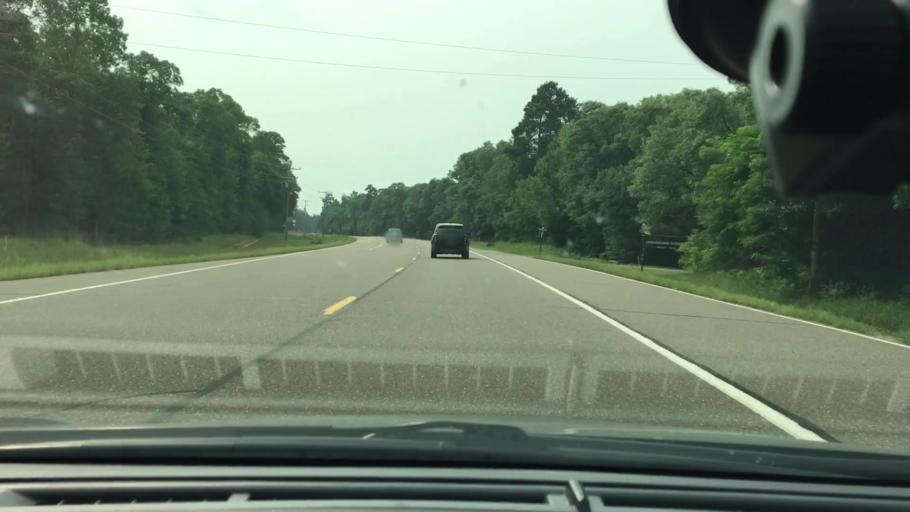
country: US
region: Minnesota
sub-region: Crow Wing County
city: Cross Lake
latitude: 46.5780
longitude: -94.1313
